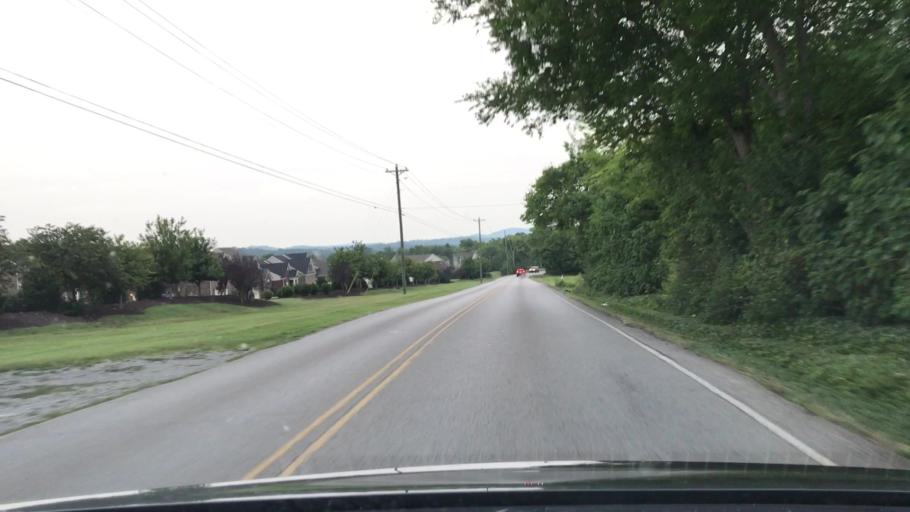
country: US
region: Tennessee
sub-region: Williamson County
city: Nolensville
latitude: 35.9491
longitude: -86.6441
